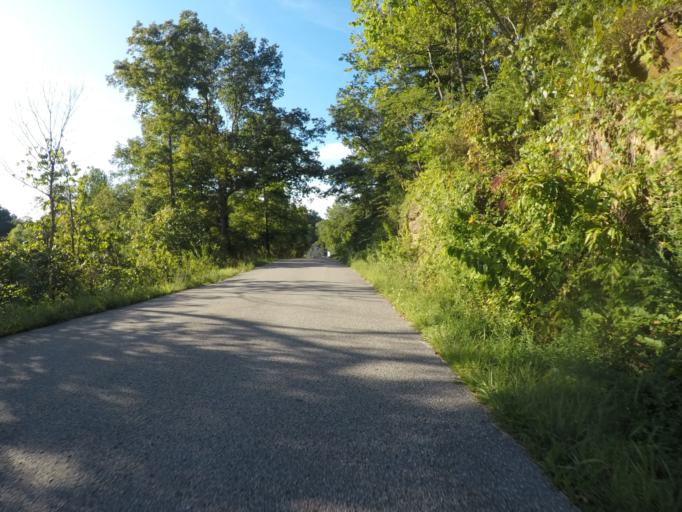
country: US
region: West Virginia
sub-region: Cabell County
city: Huntington
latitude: 38.5200
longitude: -82.5019
